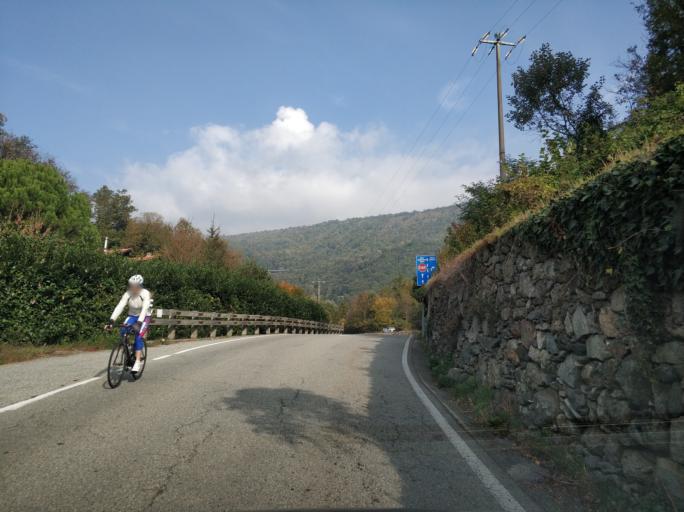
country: IT
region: Piedmont
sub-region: Provincia di Torino
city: Chiaverano
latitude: 45.5050
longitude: 7.8985
